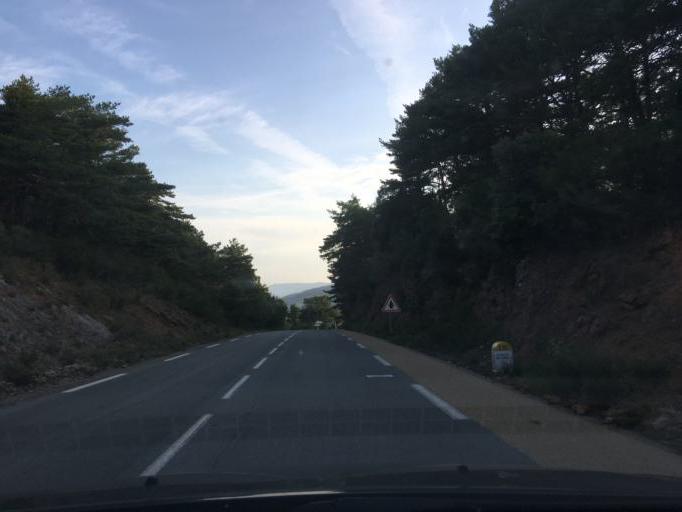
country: FR
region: Provence-Alpes-Cote d'Azur
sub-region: Departement du Var
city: Aups
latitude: 43.6630
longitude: 6.2270
